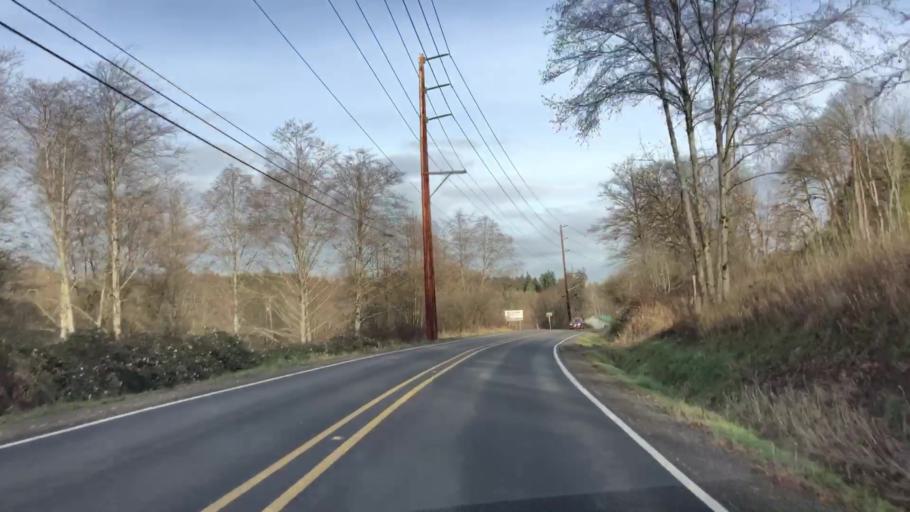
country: US
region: Washington
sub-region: Kitsap County
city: Indianola
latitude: 47.7790
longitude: -122.5549
